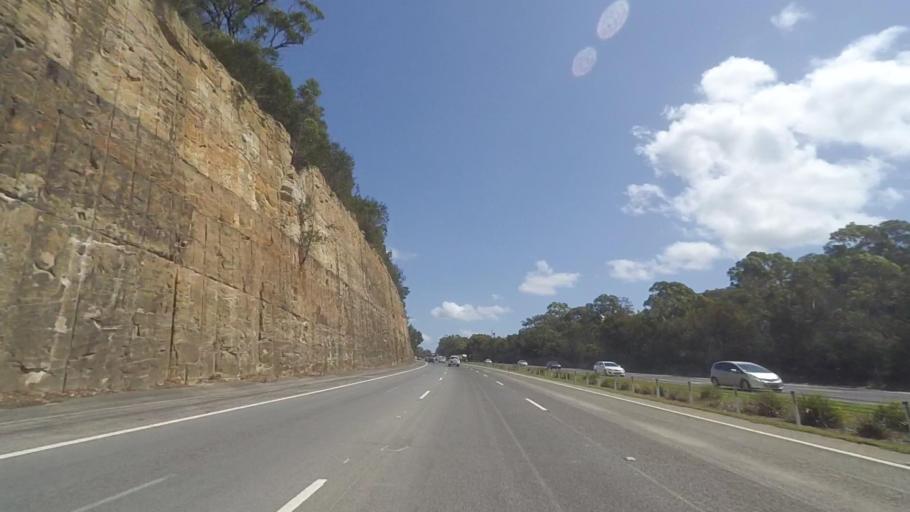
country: AU
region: New South Wales
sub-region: Hornsby Shire
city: Berowra
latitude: -33.6280
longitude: 151.1504
